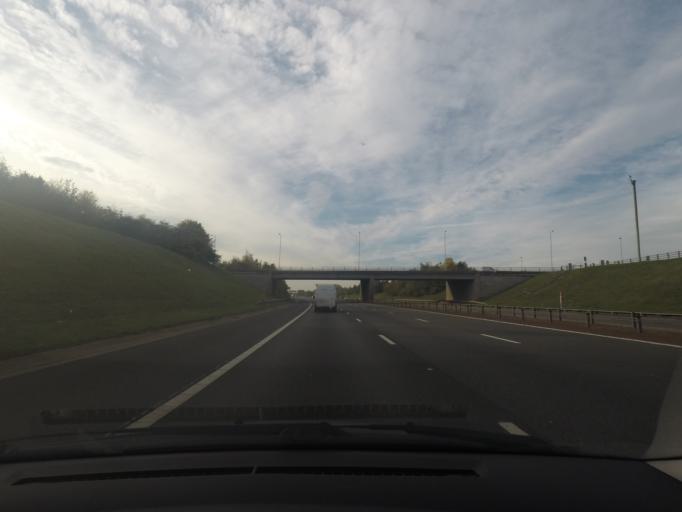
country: GB
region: England
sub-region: City and Borough of Leeds
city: Swillington
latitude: 53.7922
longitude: -1.4263
